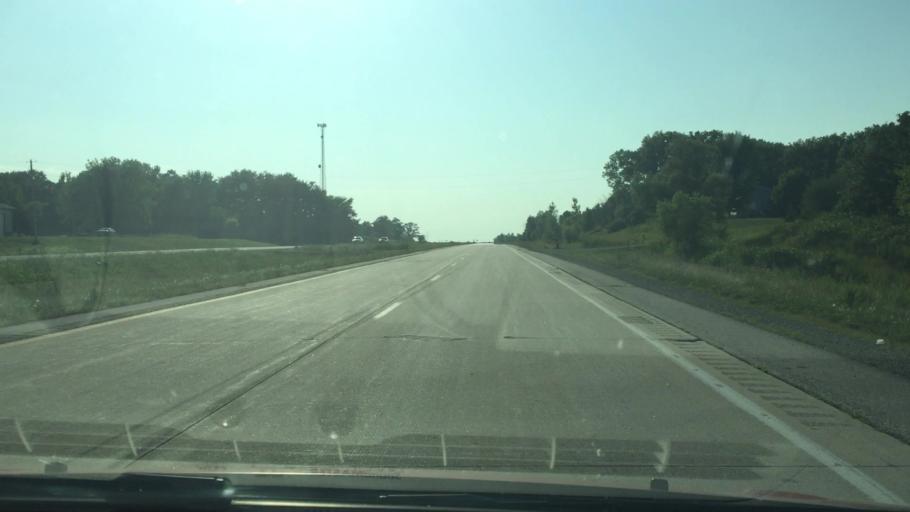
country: US
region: Iowa
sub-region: Scott County
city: Blue Grass
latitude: 41.5181
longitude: -90.8468
